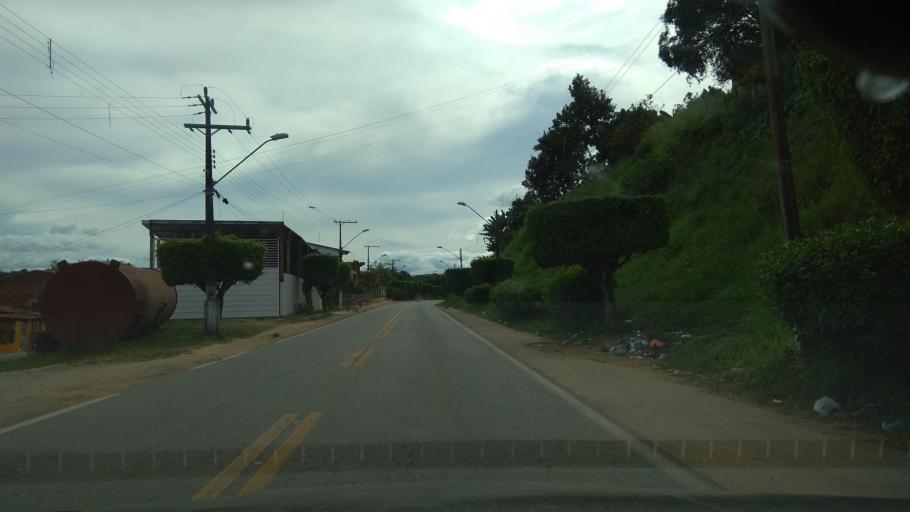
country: BR
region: Bahia
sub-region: Ubata
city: Ubata
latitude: -14.2091
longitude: -39.5263
